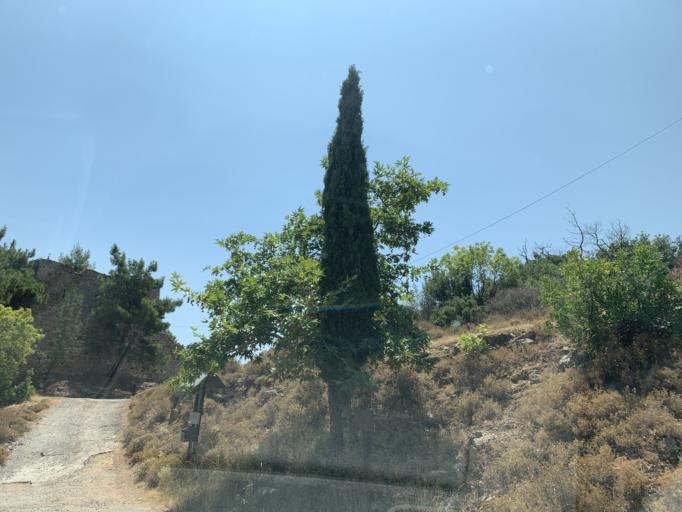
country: GR
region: North Aegean
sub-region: Chios
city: Chios
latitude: 38.3749
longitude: 26.0546
